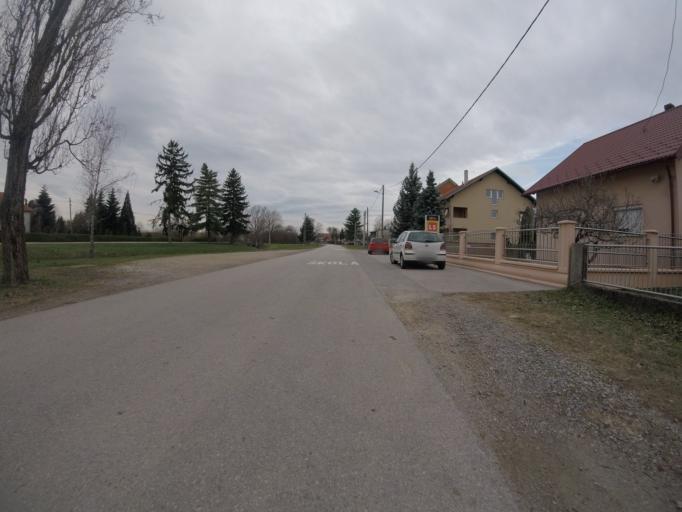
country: HR
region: Zagrebacka
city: Lukavec
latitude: 45.7008
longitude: 15.9949
